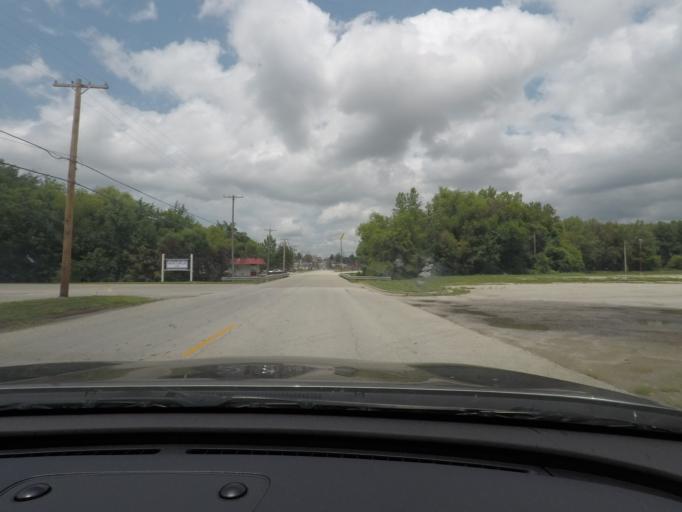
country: US
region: Missouri
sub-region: Carroll County
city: Carrollton
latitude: 39.3474
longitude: -93.4959
